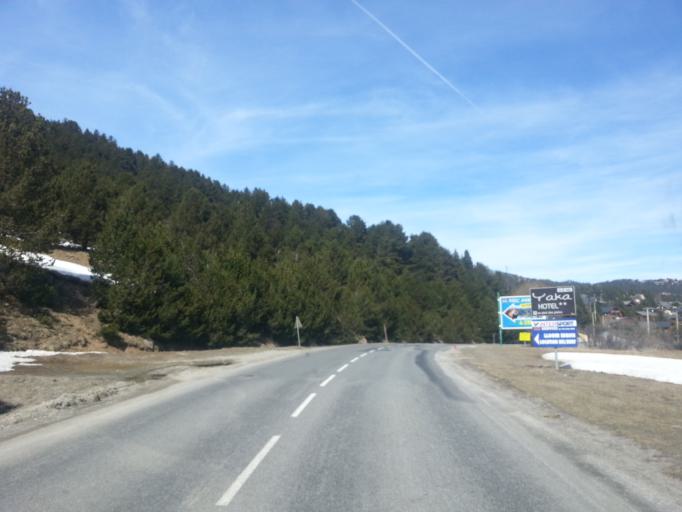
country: ES
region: Catalonia
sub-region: Provincia de Girona
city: Llivia
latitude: 42.5649
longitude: 2.0725
